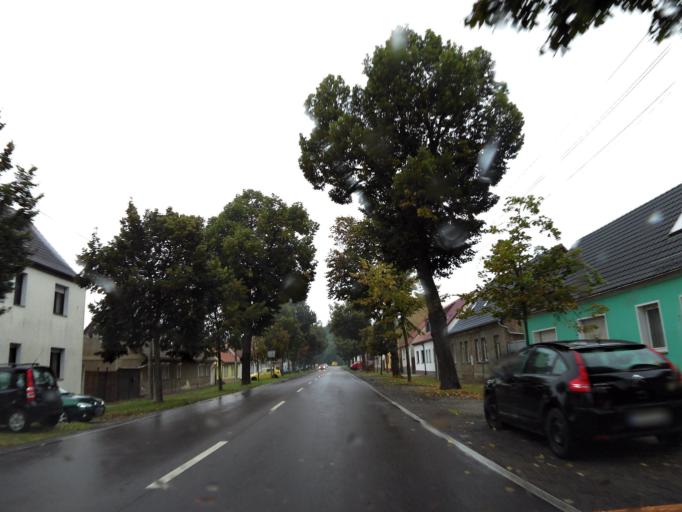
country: DE
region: Saxony-Anhalt
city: Quellendorf
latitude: 51.8040
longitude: 12.1478
